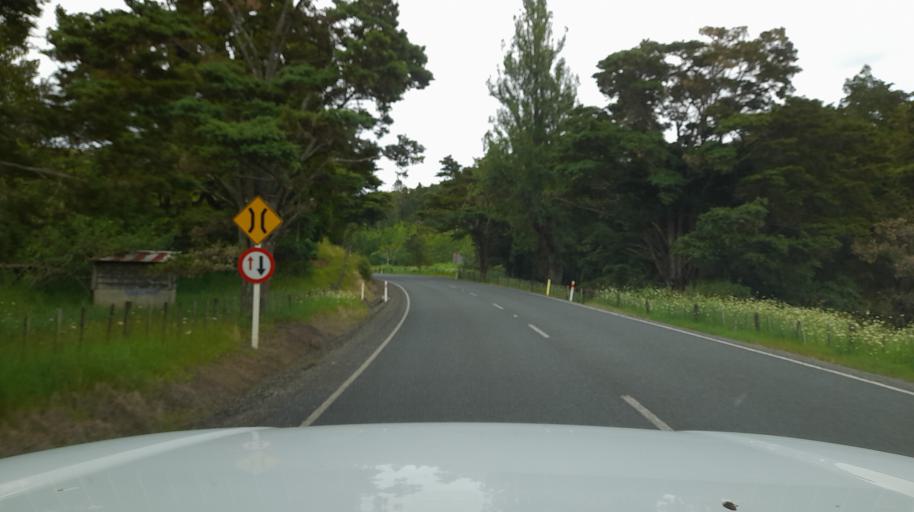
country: NZ
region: Northland
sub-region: Far North District
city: Kaitaia
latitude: -35.3035
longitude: 173.3549
